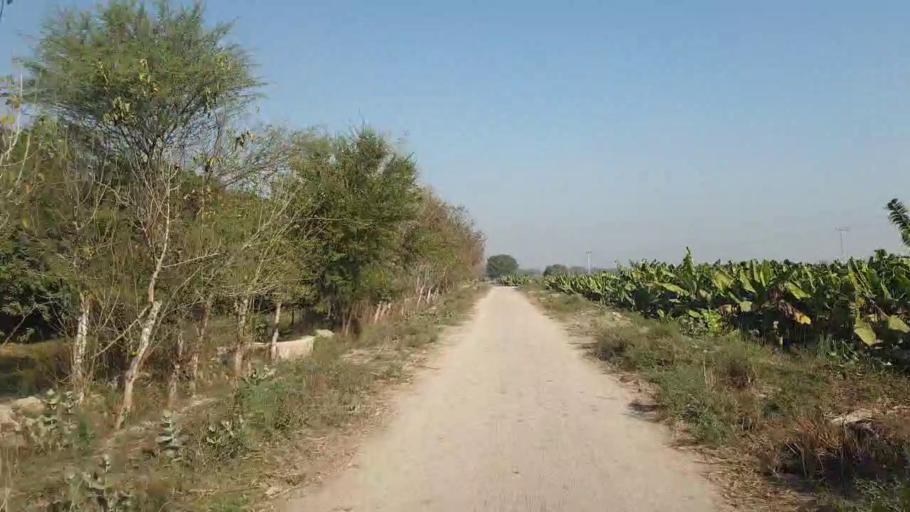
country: PK
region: Sindh
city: Tando Allahyar
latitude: 25.3675
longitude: 68.6679
